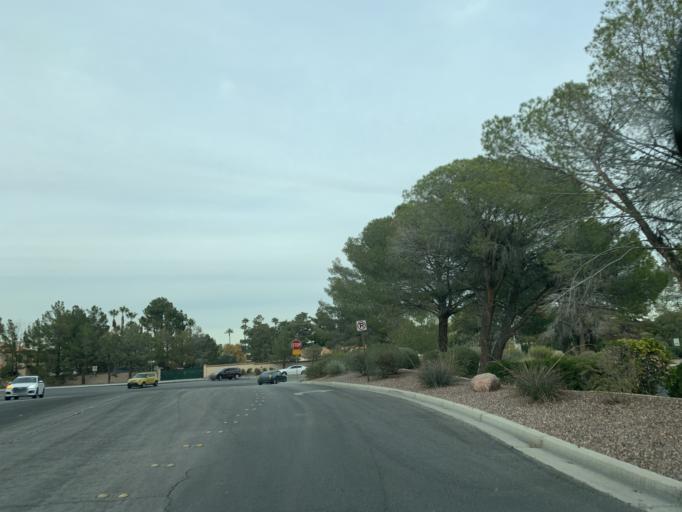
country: US
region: Nevada
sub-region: Clark County
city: Summerlin South
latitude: 36.1434
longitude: -115.2879
